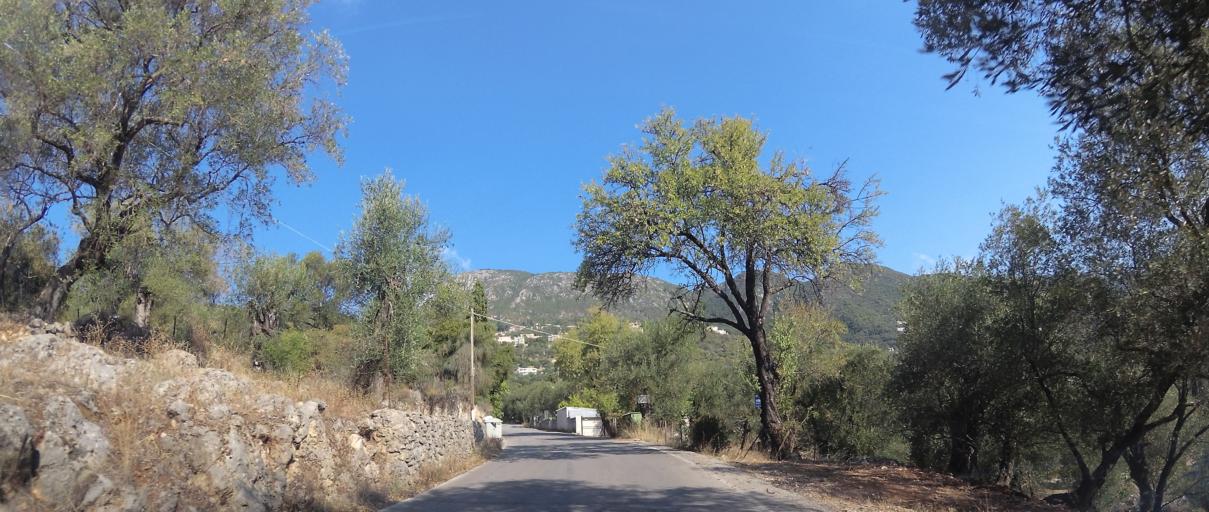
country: GR
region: Ionian Islands
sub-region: Nomos Kerkyras
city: Kontokali
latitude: 39.7125
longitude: 19.8475
